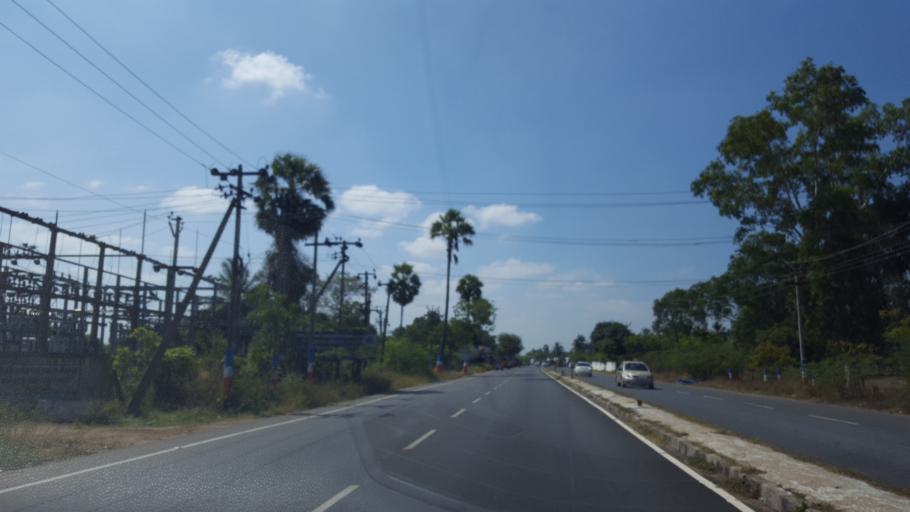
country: IN
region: Tamil Nadu
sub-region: Kancheepuram
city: Mamallapuram
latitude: 12.6965
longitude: 80.1820
